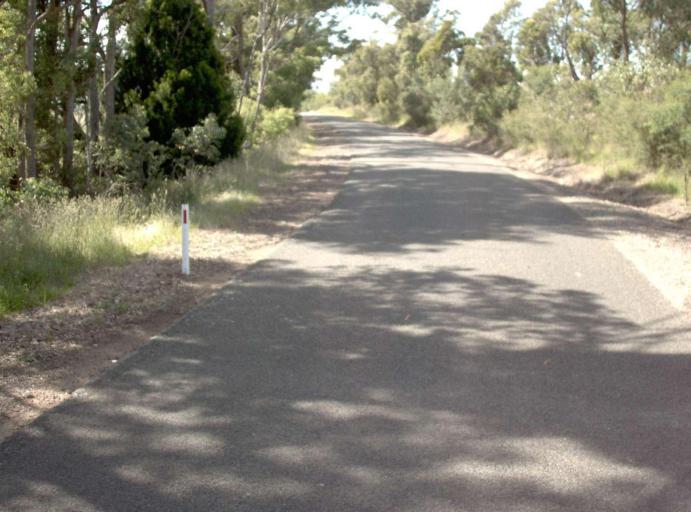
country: AU
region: Victoria
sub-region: East Gippsland
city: Lakes Entrance
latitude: -37.4920
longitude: 148.1307
